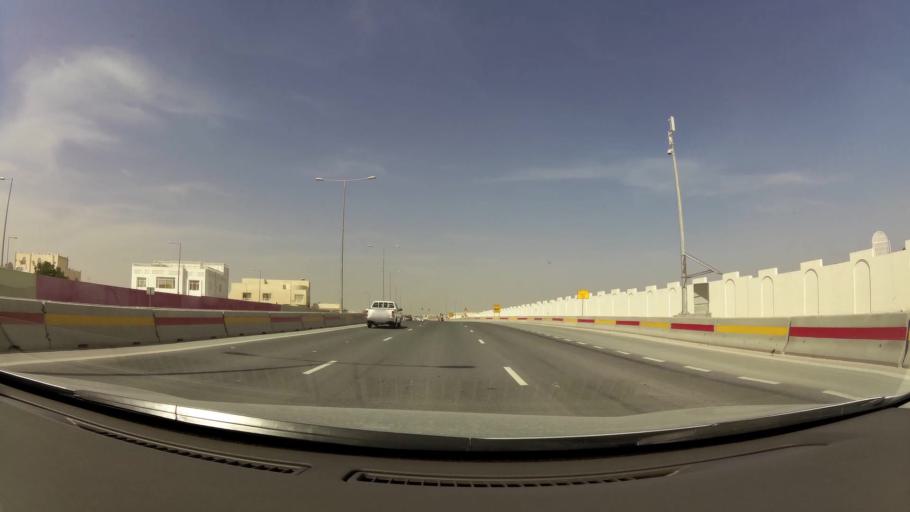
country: QA
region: Baladiyat ar Rayyan
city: Ar Rayyan
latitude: 25.3144
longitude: 51.4167
